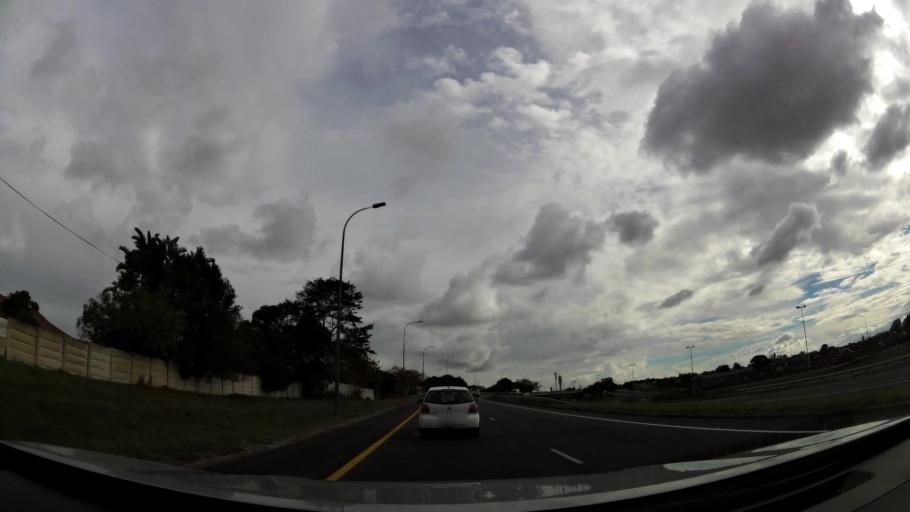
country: ZA
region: Eastern Cape
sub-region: Nelson Mandela Bay Metropolitan Municipality
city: Port Elizabeth
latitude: -33.9469
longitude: 25.5295
